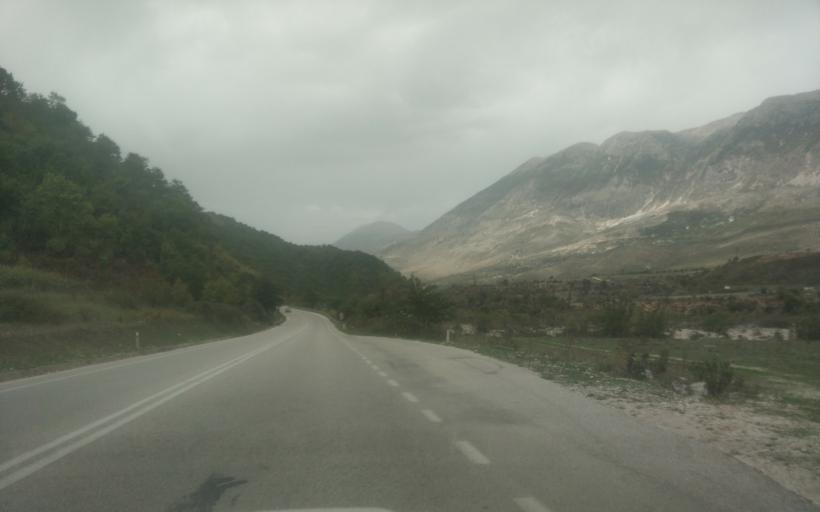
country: AL
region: Gjirokaster
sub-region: Rrethi i Gjirokastres
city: Picar
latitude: 40.2109
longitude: 20.0884
